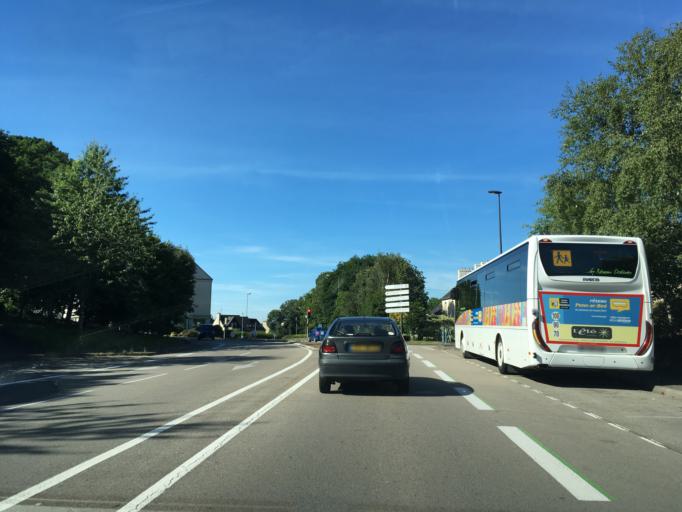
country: FR
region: Brittany
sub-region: Departement du Finistere
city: Quimper
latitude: 47.9845
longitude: -4.0755
